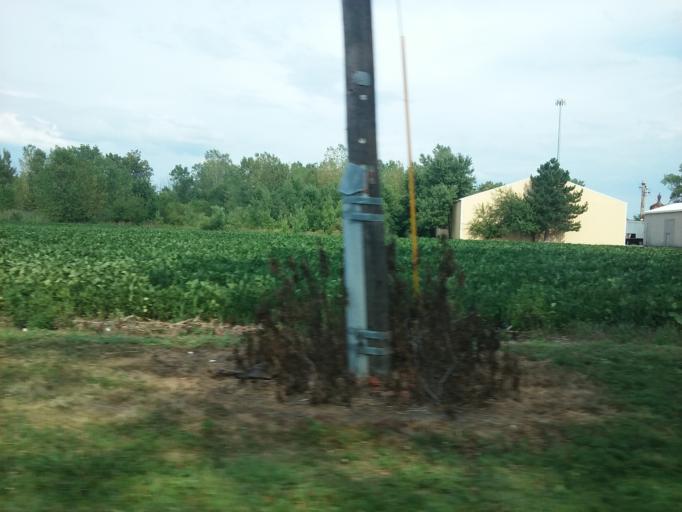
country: US
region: Ohio
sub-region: Hancock County
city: McComb
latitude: 41.1932
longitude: -83.7844
